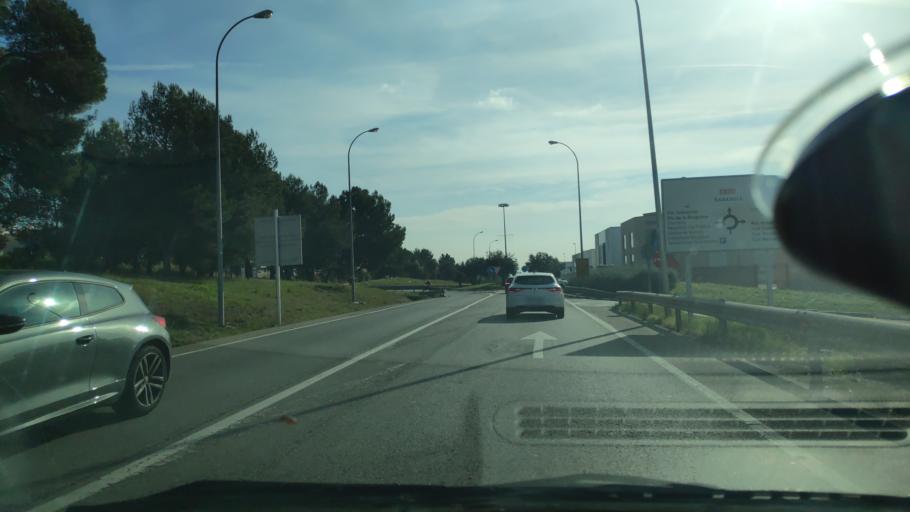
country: ES
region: Catalonia
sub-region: Provincia de Barcelona
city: Castellar del Valles
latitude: 41.6020
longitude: 2.0859
